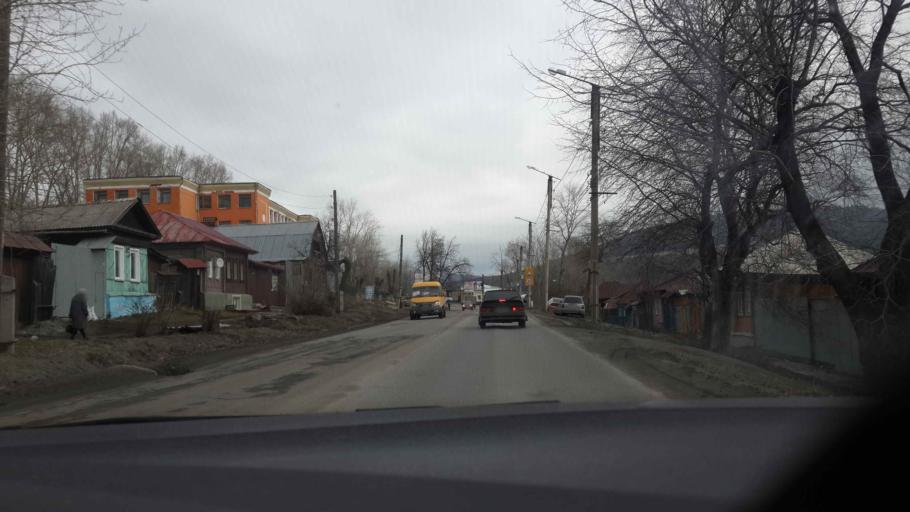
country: RU
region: Chelyabinsk
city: Zlatoust
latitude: 55.1772
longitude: 59.6980
